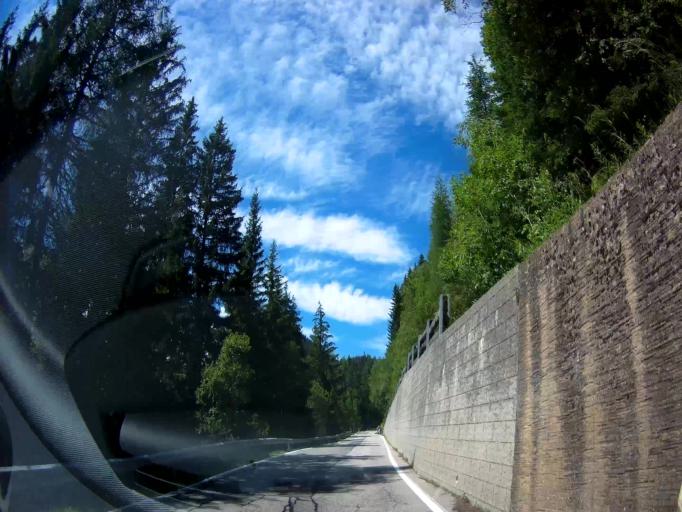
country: AT
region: Carinthia
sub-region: Politischer Bezirk Sankt Veit an der Glan
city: Glodnitz
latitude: 46.9301
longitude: 14.0542
